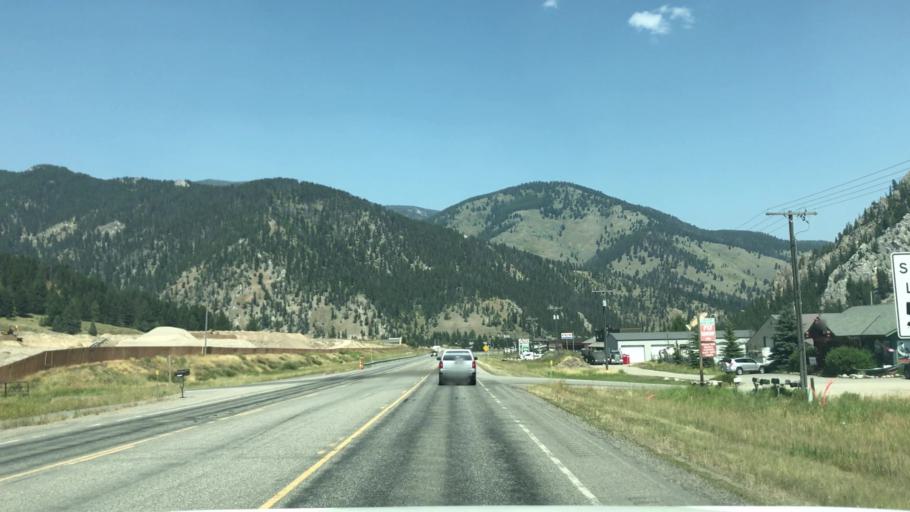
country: US
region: Montana
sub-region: Gallatin County
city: Big Sky
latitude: 45.2563
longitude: -111.2544
